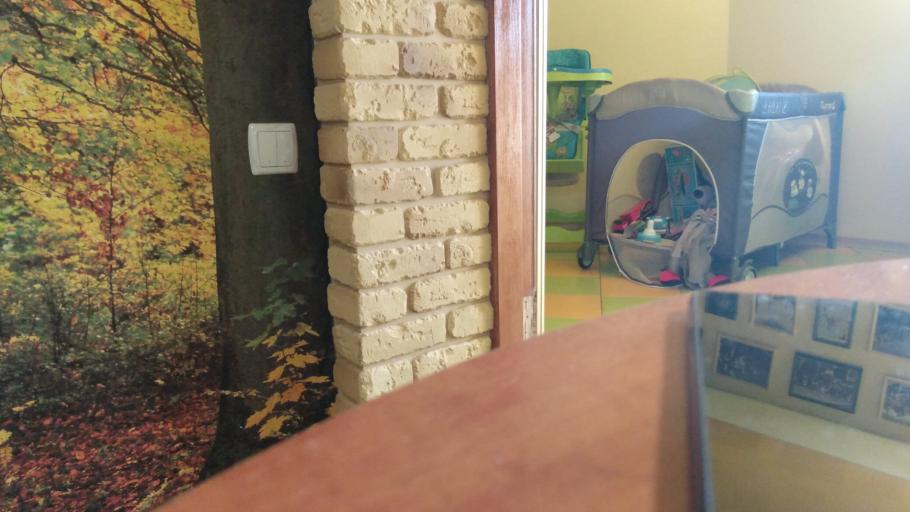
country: RU
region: Tverskaya
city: Bologoye
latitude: 57.8742
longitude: 34.3024
